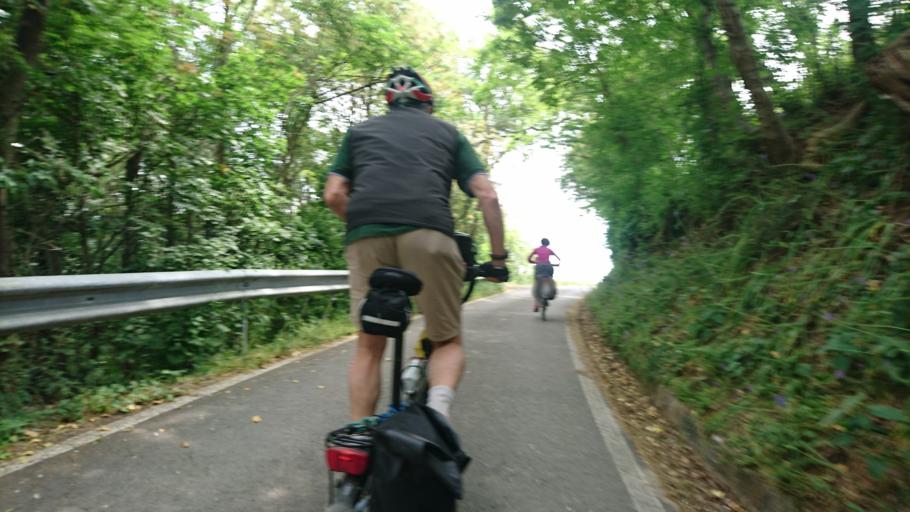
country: IT
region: Veneto
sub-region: Provincia di Padova
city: Arqua Petrarca
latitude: 45.2617
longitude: 11.7063
